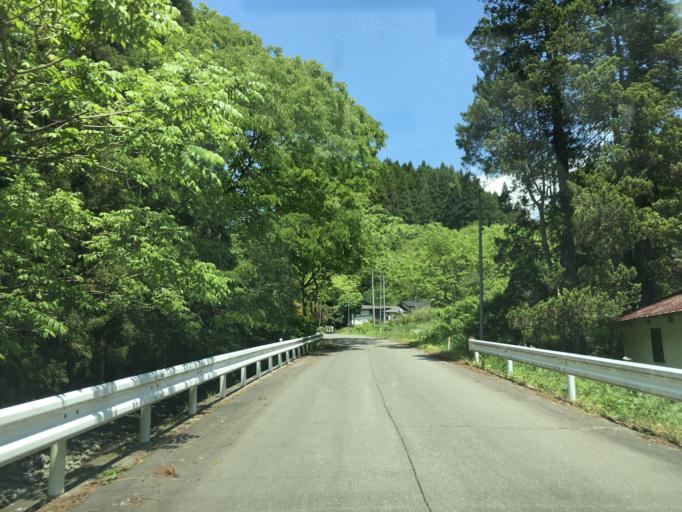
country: JP
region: Miyagi
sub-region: Oshika Gun
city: Onagawa Cho
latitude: 38.6747
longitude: 141.3632
